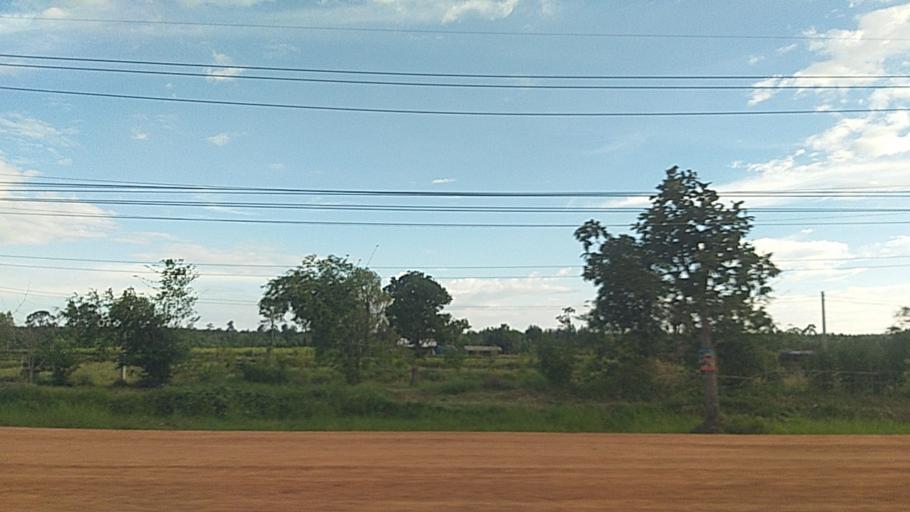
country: TH
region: Surin
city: Kap Choeng
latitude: 14.4571
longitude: 103.6737
